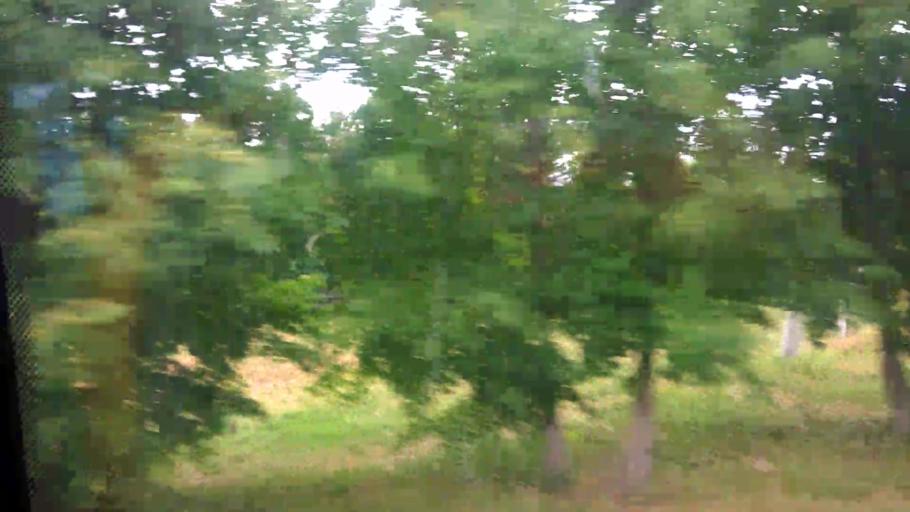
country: RU
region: Moskovskaya
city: Ozery
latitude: 54.7723
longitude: 38.6406
